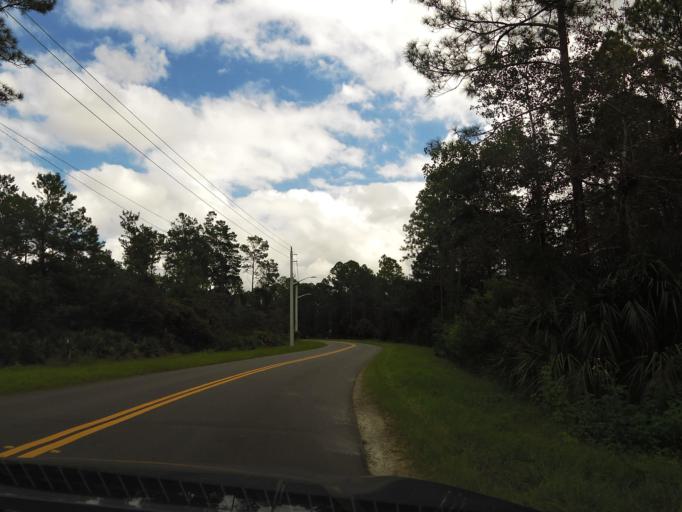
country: US
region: Florida
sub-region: Saint Johns County
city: Palm Valley
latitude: 30.0456
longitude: -81.4048
